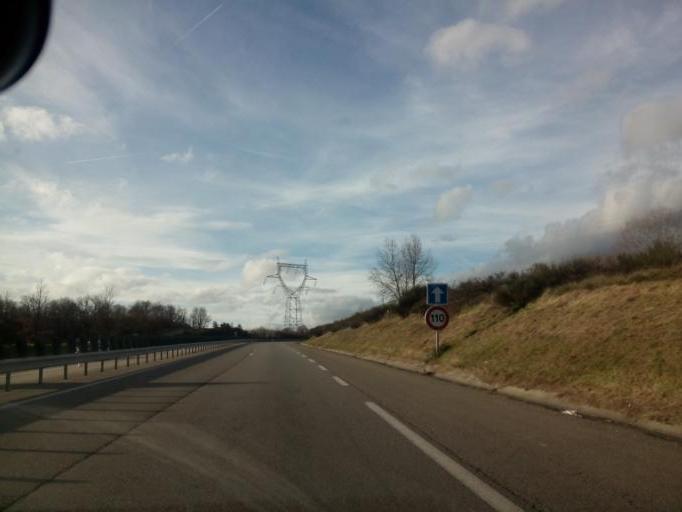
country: FR
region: Rhone-Alpes
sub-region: Departement de l'Ardeche
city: Felines
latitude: 45.3070
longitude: 4.7401
